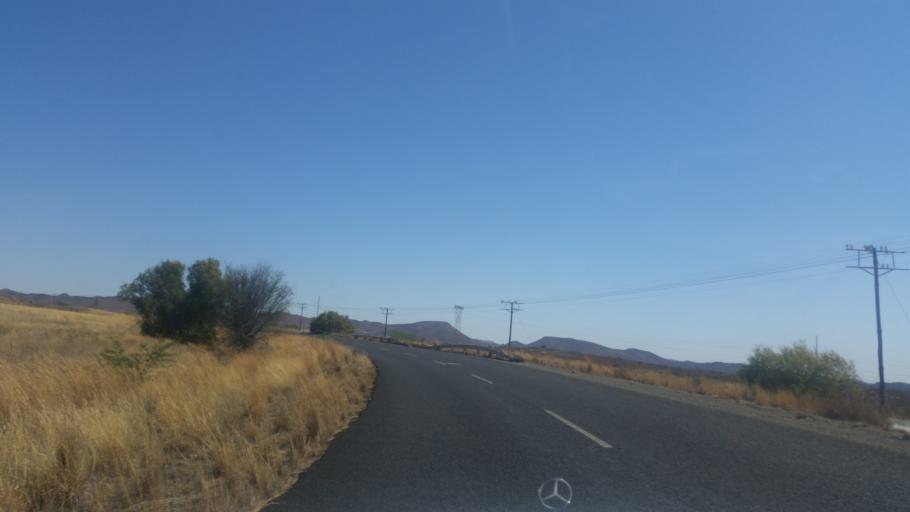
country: ZA
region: Northern Cape
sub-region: Pixley ka Seme District Municipality
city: Colesberg
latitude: -30.5983
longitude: 25.4818
